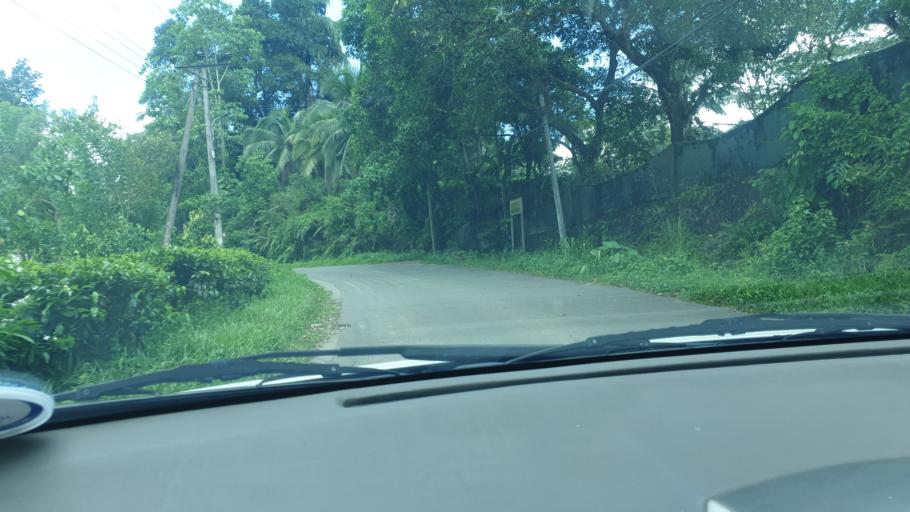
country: LK
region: Sabaragamuwa
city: Ratnapura
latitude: 6.4906
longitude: 80.3992
